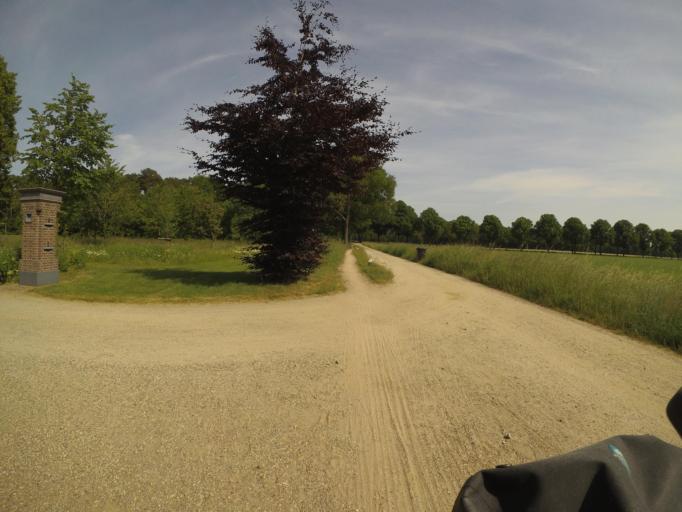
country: NL
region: Gelderland
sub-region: Gemeente Aalten
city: Bredevoort
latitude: 51.9341
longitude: 6.6696
